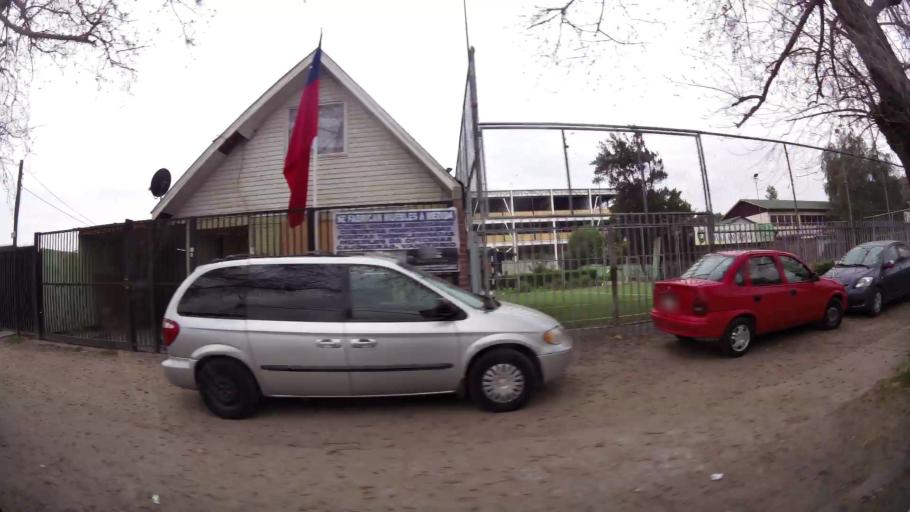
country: CL
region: Santiago Metropolitan
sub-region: Provincia de Santiago
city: Lo Prado
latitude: -33.5029
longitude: -70.7640
